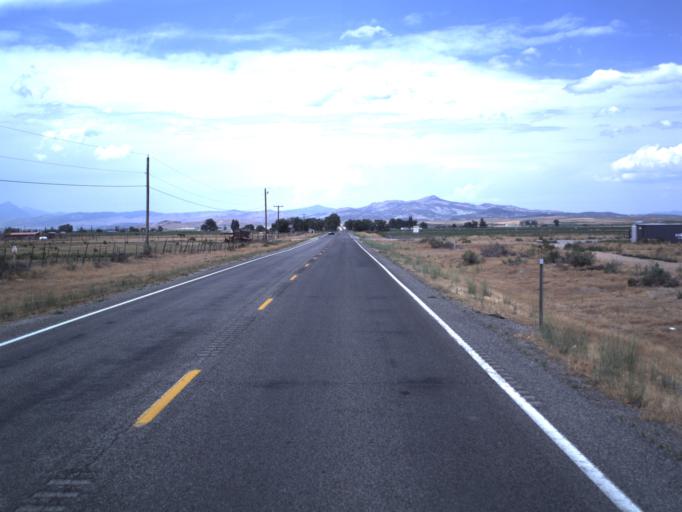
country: US
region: Utah
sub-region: Sanpete County
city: Moroni
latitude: 39.4596
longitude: -111.5626
